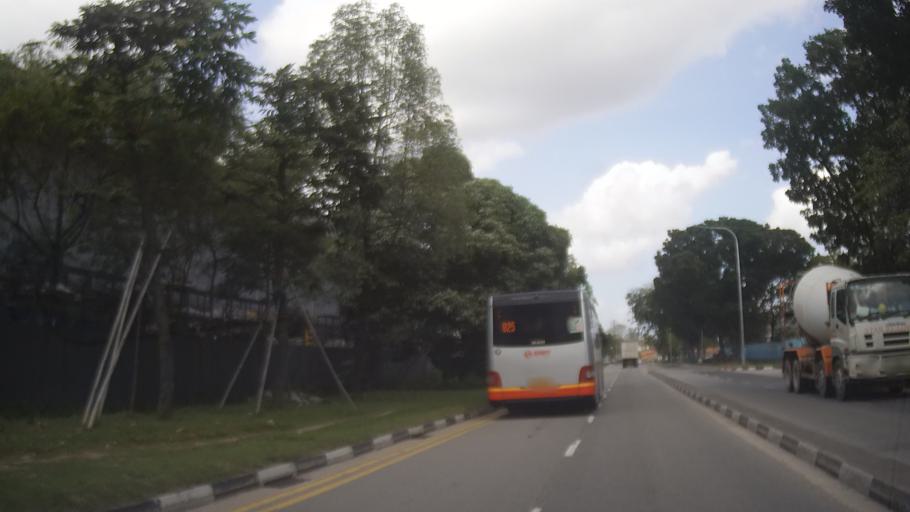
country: MY
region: Johor
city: Johor Bahru
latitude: 1.4328
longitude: 103.7480
